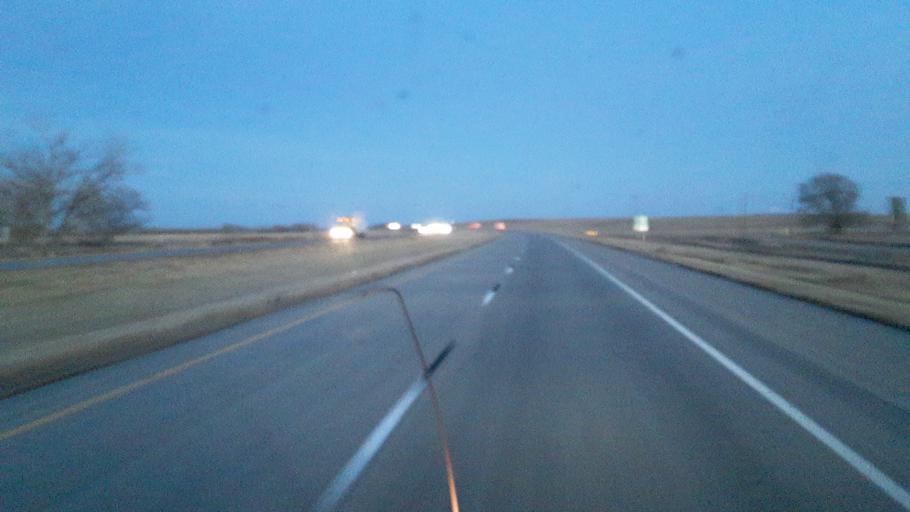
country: US
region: Nebraska
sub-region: Keith County
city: Ogallala
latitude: 41.1044
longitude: -101.4834
